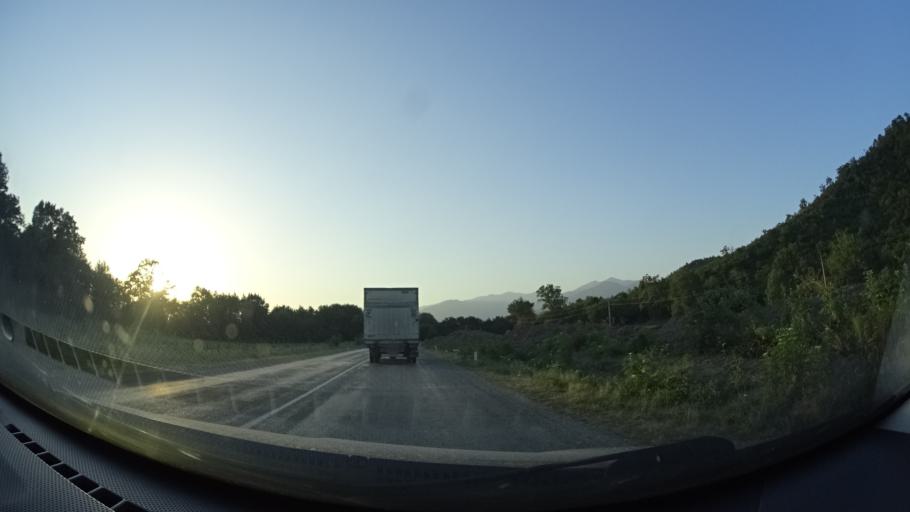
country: GE
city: Bagdadi
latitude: 41.8560
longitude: 46.0287
